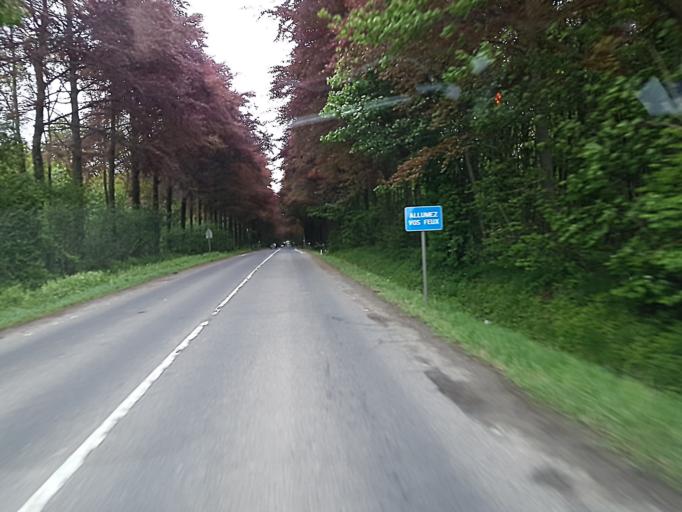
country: BE
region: Wallonia
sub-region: Province du Brabant Wallon
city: Walhain-Saint-Paul
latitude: 50.6056
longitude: 4.7402
